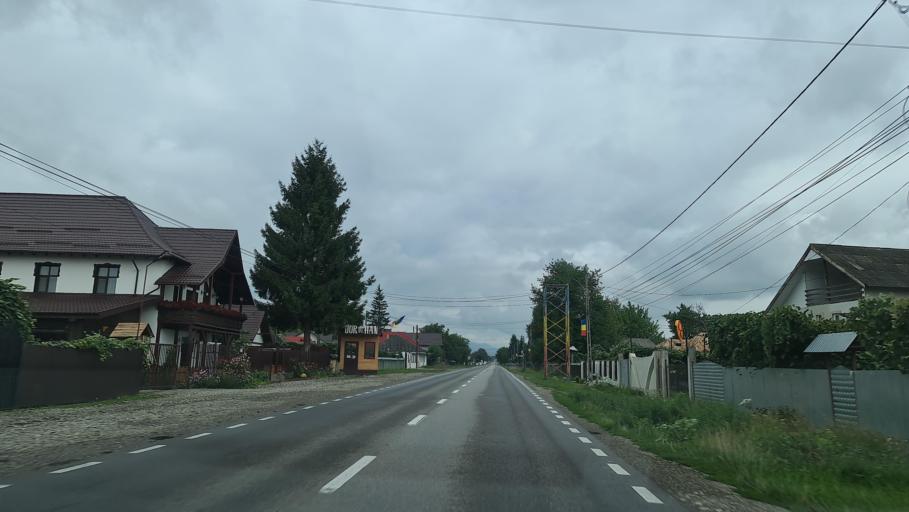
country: RO
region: Neamt
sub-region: Comuna Roznov
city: Roznov
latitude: 46.8143
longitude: 26.5120
